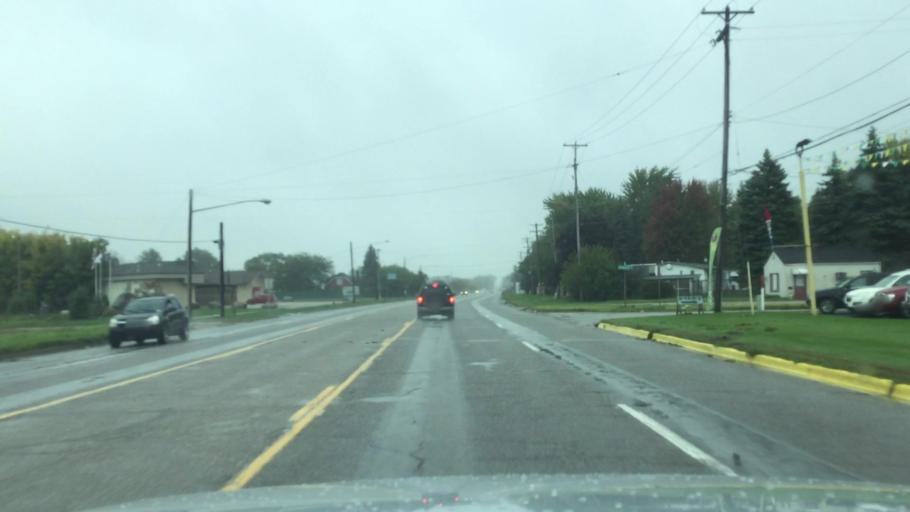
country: US
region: Michigan
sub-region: Saginaw County
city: Buena Vista
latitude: 43.3925
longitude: -83.9067
